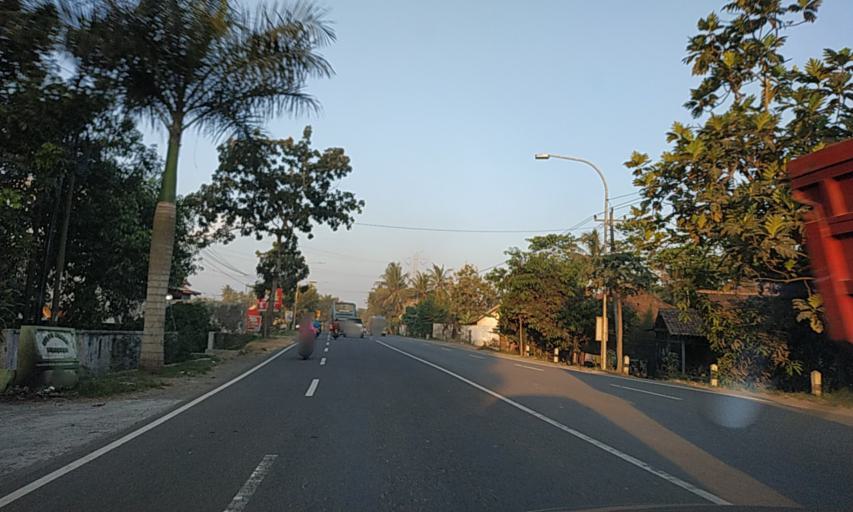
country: ID
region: Daerah Istimewa Yogyakarta
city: Srandakan
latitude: -7.8868
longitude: 110.0538
